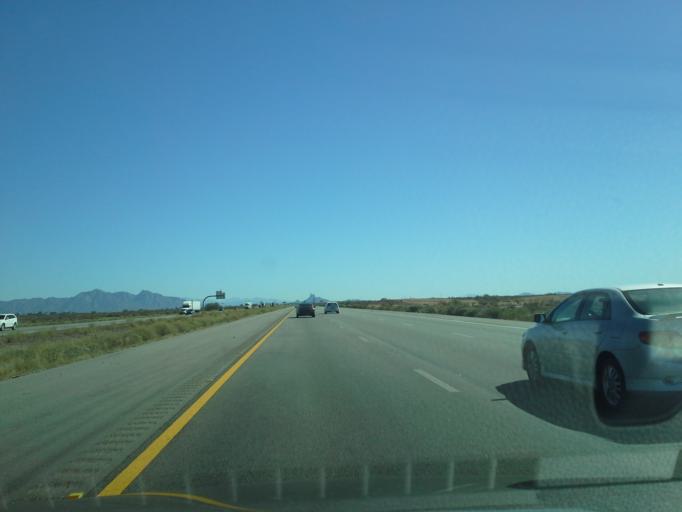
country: US
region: Arizona
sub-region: Pinal County
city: Arizona City
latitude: 32.7967
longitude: -111.6511
